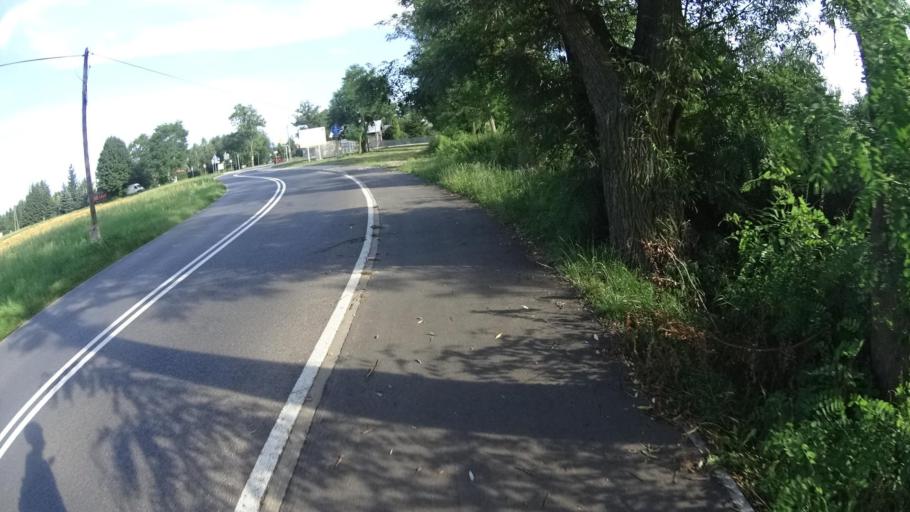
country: PL
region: Masovian Voivodeship
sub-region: Powiat piaseczynski
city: Tarczyn
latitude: 52.0237
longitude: 20.7851
